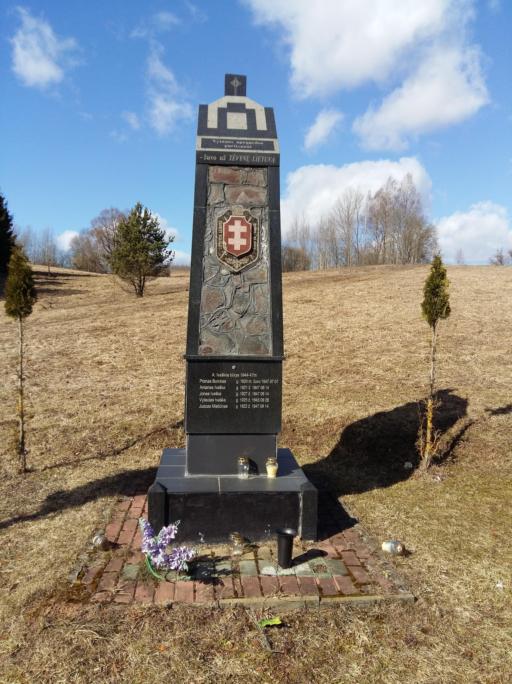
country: LT
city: Zarasai
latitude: 55.8426
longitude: 26.1286
